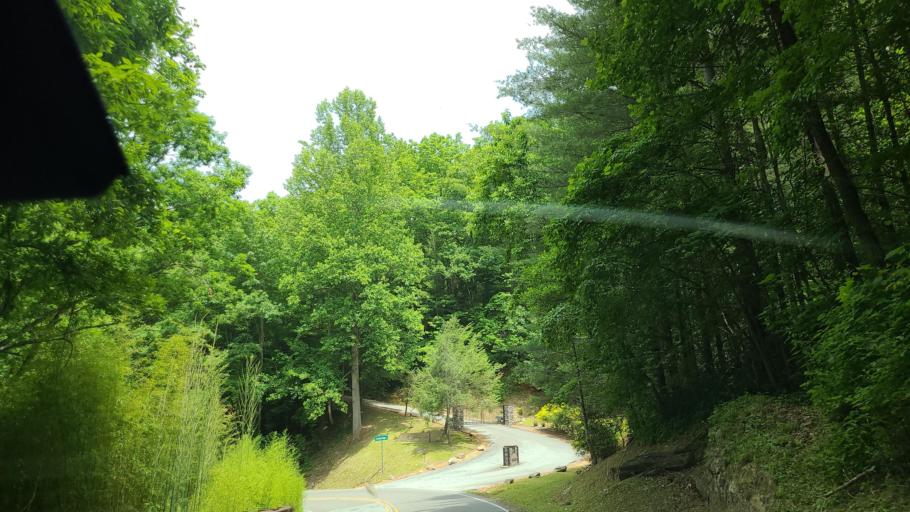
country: US
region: North Carolina
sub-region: Macon County
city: Franklin
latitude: 35.1235
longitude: -83.2788
